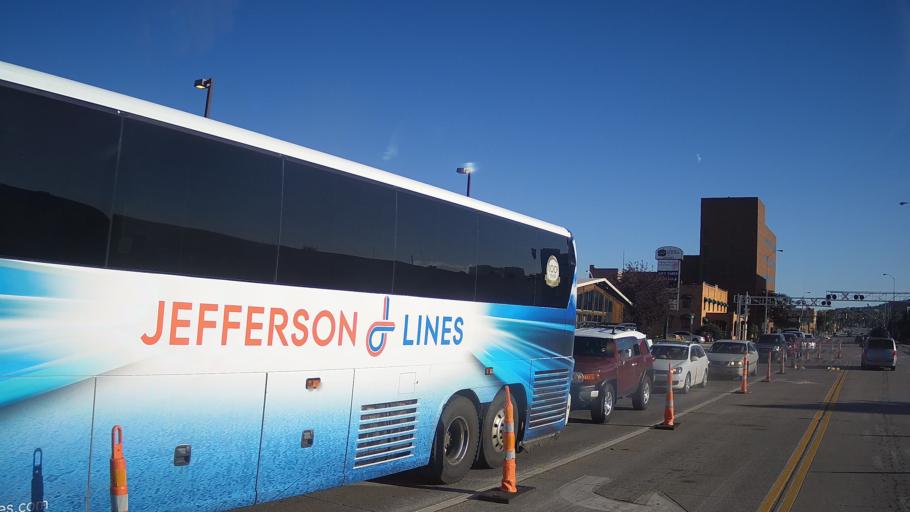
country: US
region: South Dakota
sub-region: Pennington County
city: Rapid City
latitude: 44.0838
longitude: -103.2301
